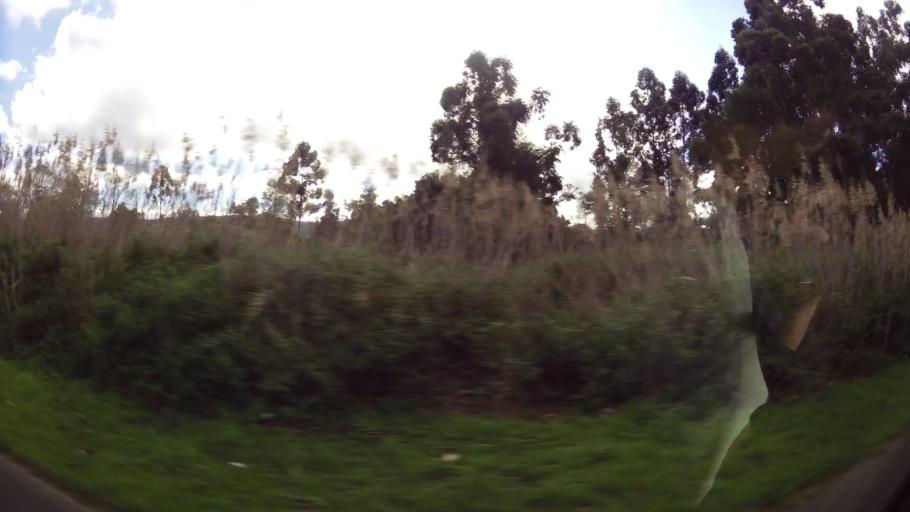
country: ZA
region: Western Cape
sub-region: Eden District Municipality
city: Knysna
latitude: -34.0542
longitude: 23.0745
